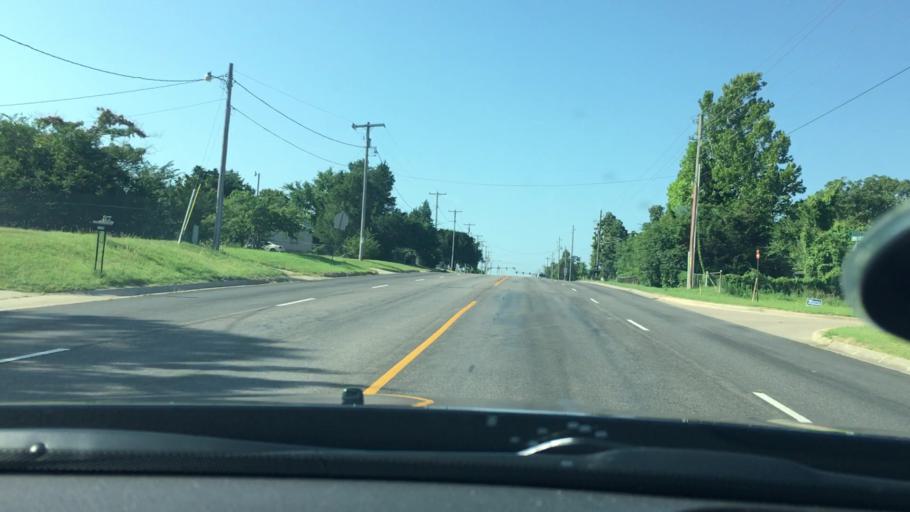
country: US
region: Oklahoma
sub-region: Pontotoc County
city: Ada
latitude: 34.7855
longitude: -96.6349
